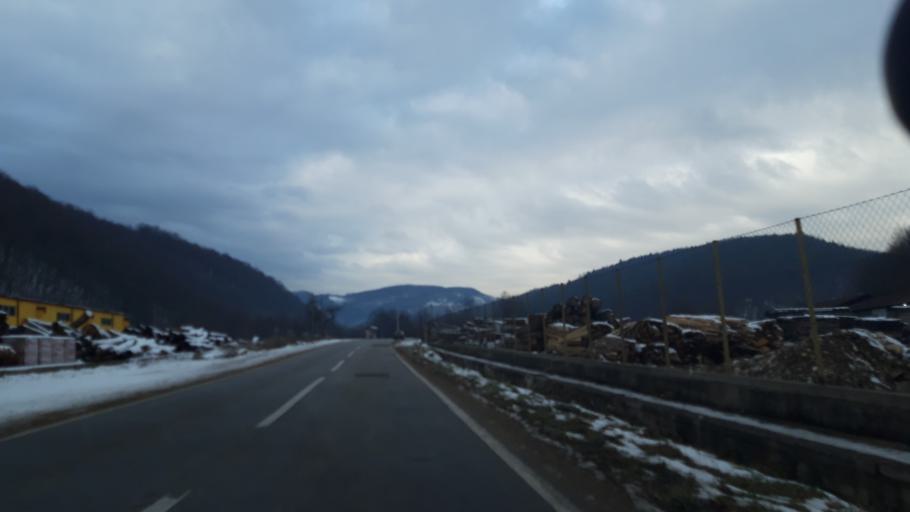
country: BA
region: Republika Srpska
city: Milici
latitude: 44.1661
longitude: 19.0373
